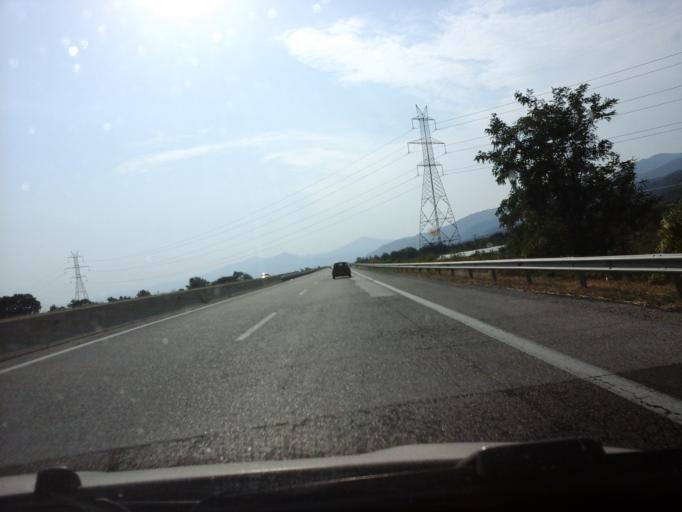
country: GR
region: East Macedonia and Thrace
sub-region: Nomos Rodopis
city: Iasmos
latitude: 41.1180
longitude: 25.1005
